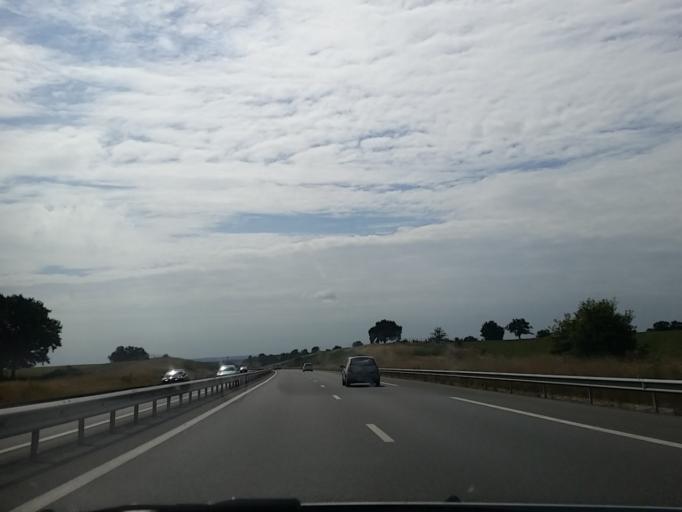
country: FR
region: Auvergne
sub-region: Departement de l'Allier
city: Vallon-en-Sully
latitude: 46.5807
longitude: 2.5262
